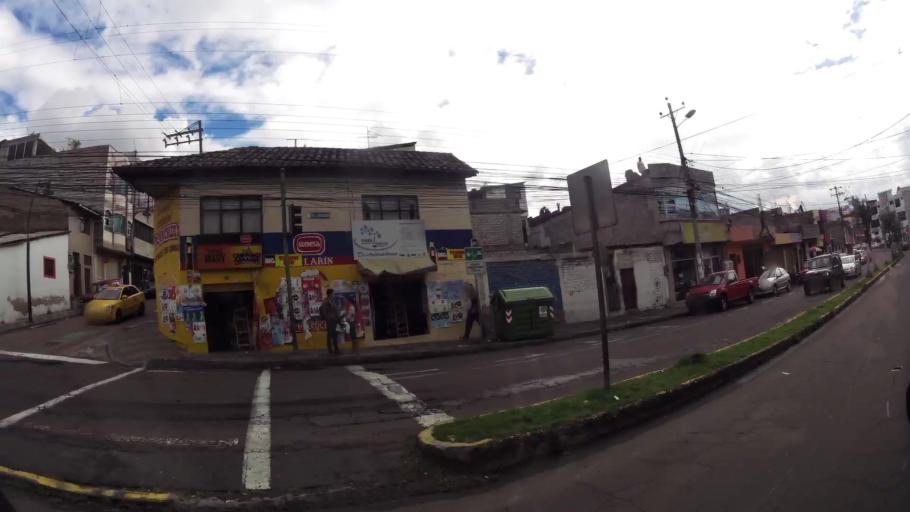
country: EC
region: Pichincha
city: Sangolqui
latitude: -0.3261
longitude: -78.4470
